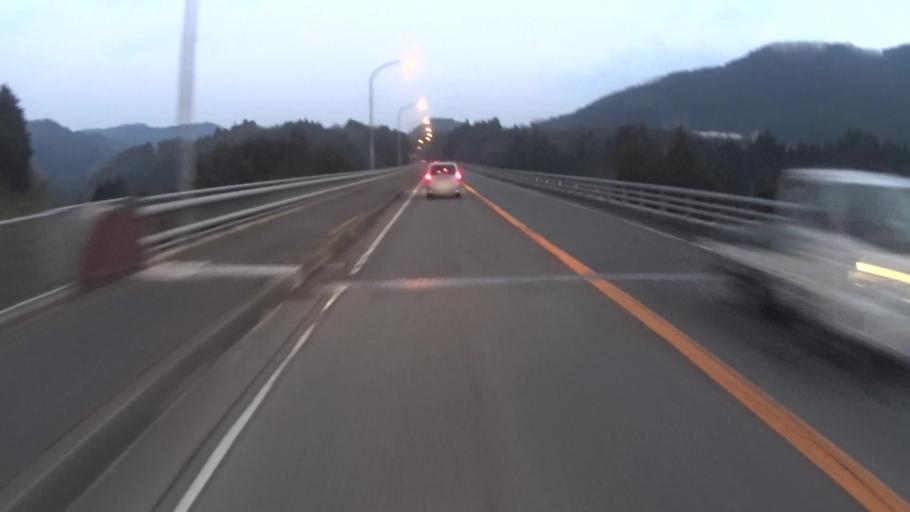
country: JP
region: Kyoto
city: Ayabe
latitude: 35.2742
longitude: 135.3511
